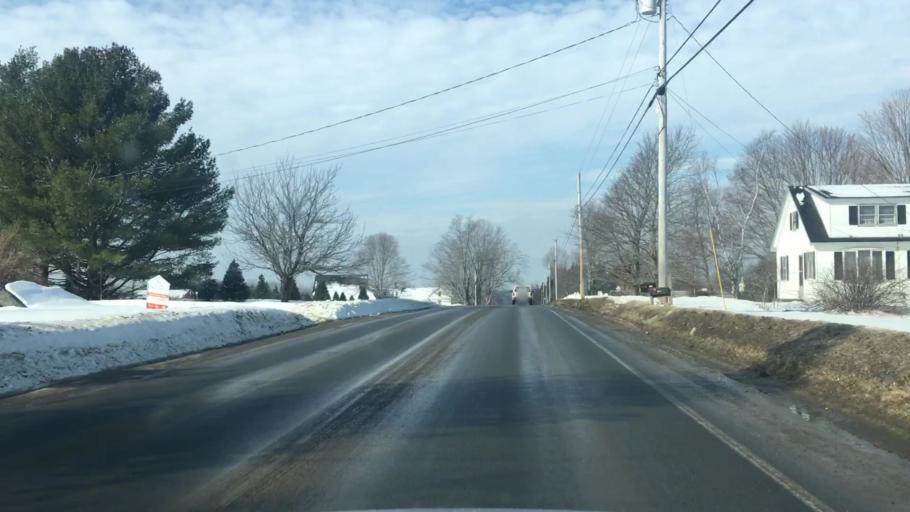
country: US
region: Maine
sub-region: Penobscot County
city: Hermon
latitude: 44.8464
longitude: -68.8703
